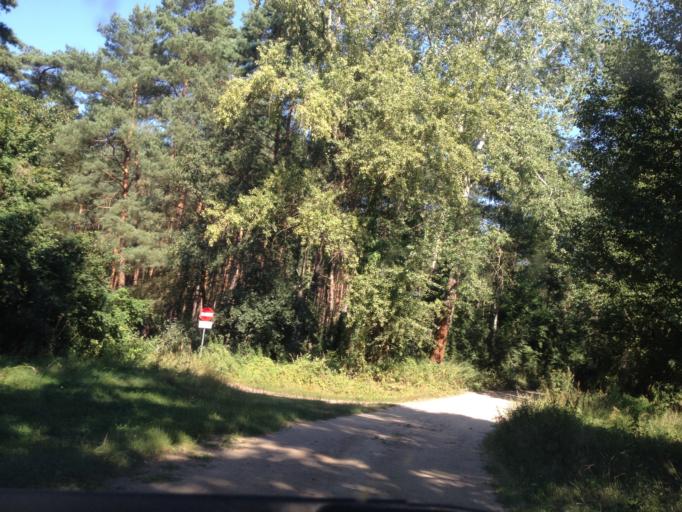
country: PL
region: Greater Poland Voivodeship
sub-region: Powiat sredzki
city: Zaniemysl
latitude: 52.1030
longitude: 17.1325
